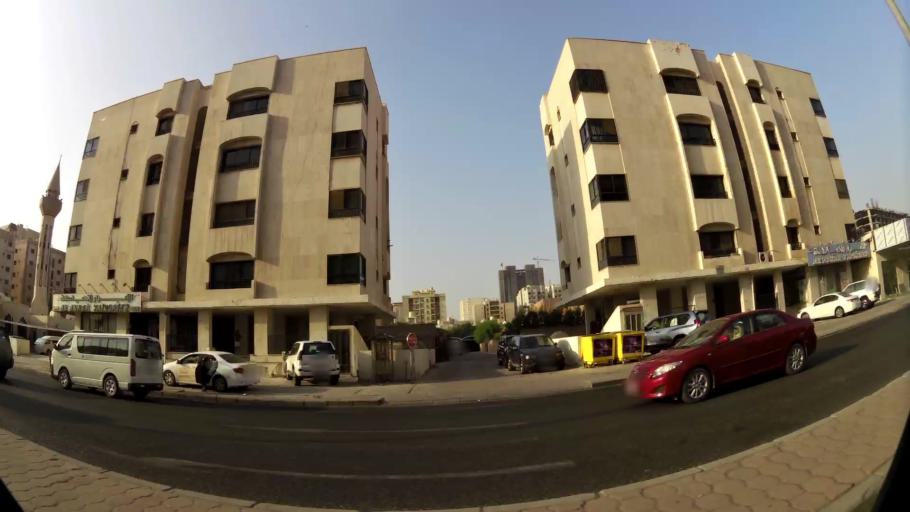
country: KW
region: Muhafazat Hawalli
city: As Salimiyah
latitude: 29.3318
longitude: 48.0590
